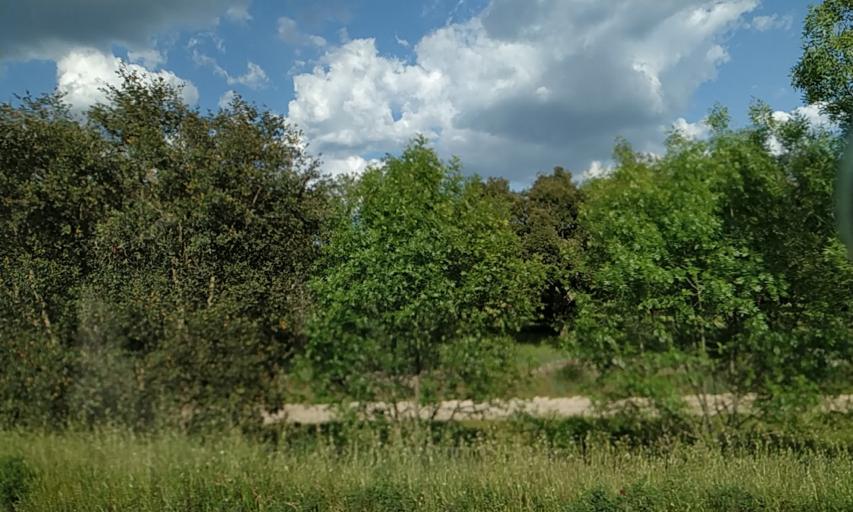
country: PT
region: Portalegre
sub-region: Portalegre
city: Urra
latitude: 39.2208
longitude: -7.4574
